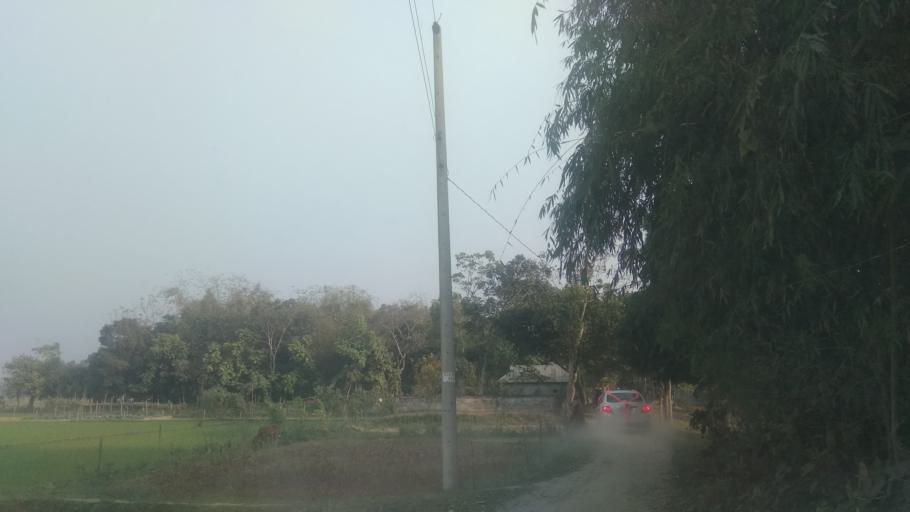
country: BD
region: Dhaka
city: Netrakona
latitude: 24.7729
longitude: 90.6118
